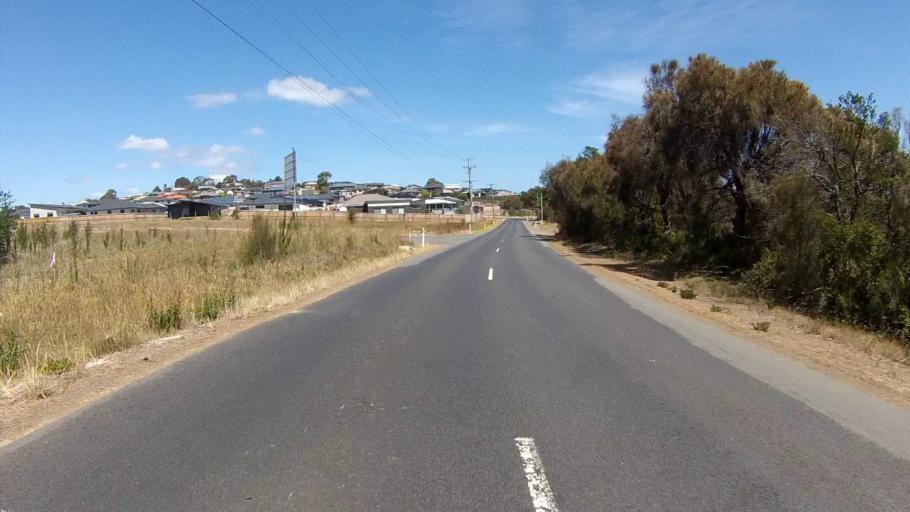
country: AU
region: Tasmania
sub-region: Sorell
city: Sorell
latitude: -42.7911
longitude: 147.5242
